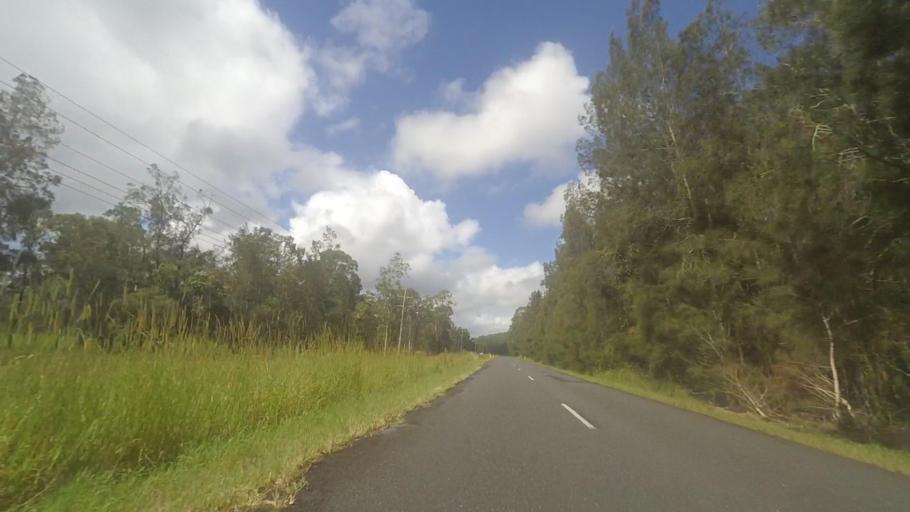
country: AU
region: New South Wales
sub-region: Great Lakes
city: Bulahdelah
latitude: -32.3892
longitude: 152.3323
